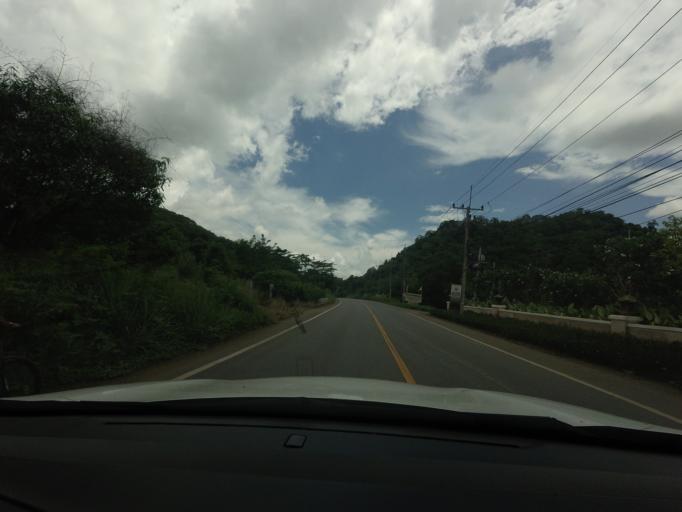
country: TH
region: Sara Buri
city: Muak Lek
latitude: 14.5596
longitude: 101.3023
